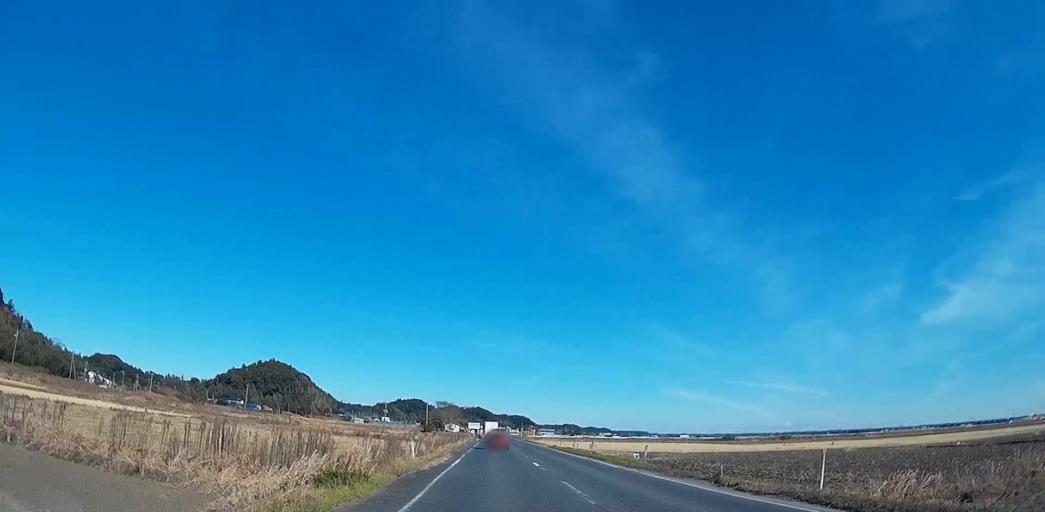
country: JP
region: Chiba
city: Yokaichiba
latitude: 35.7451
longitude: 140.5685
